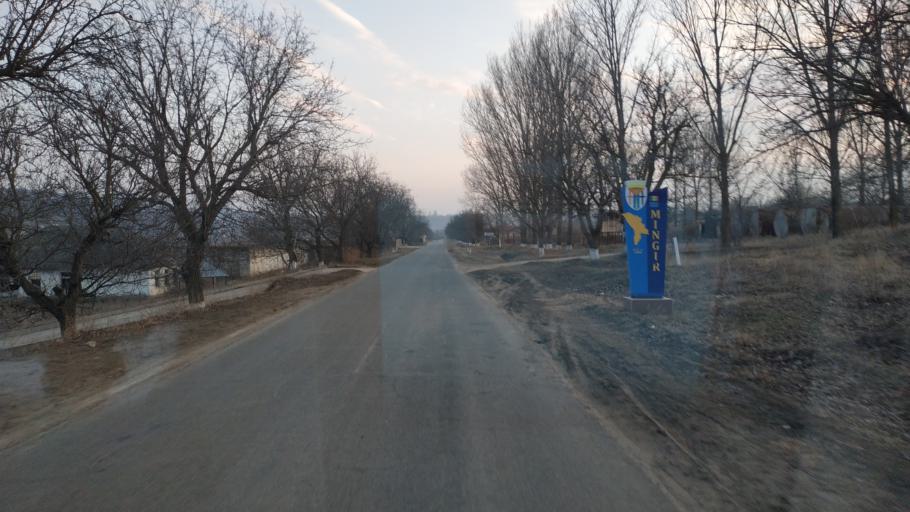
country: MD
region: Hincesti
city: Dancu
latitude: 46.6802
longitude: 28.3353
